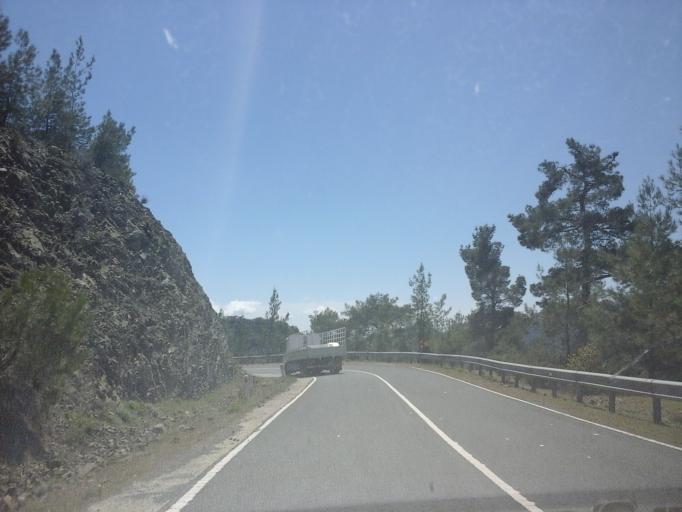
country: CY
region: Lefkosia
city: Kakopetria
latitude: 34.9997
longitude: 32.7911
